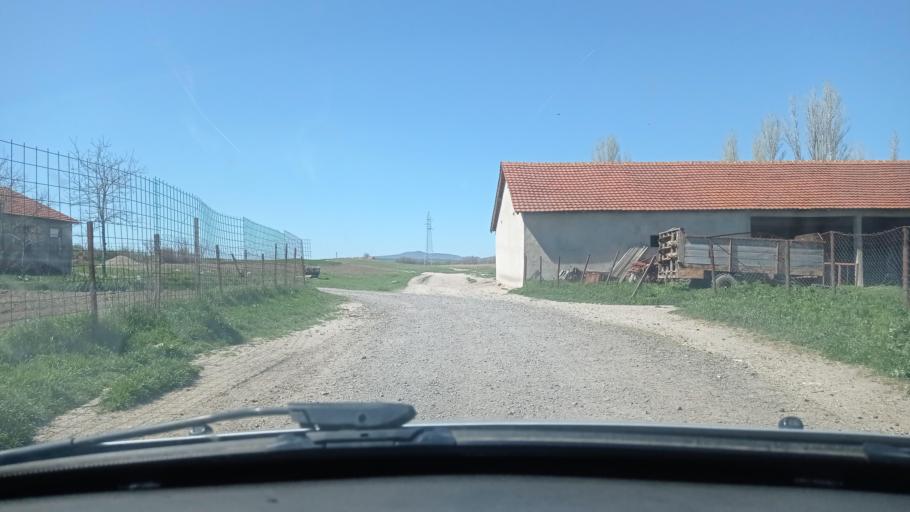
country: MK
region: Lozovo
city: Lozovo
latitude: 41.8010
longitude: 21.9410
